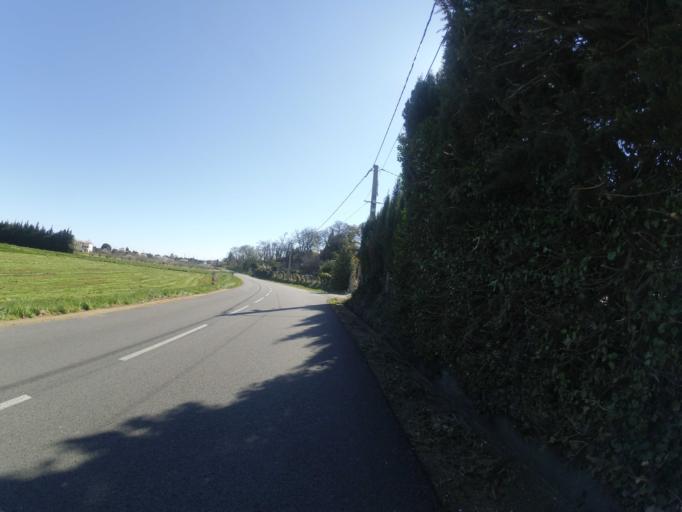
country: FR
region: Languedoc-Roussillon
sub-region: Departement des Pyrenees-Orientales
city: Ille-sur-Tet
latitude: 42.6556
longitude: 2.6173
